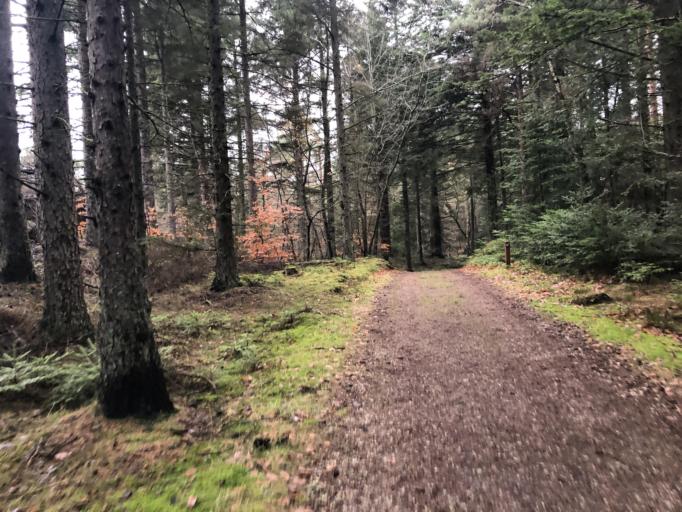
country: DK
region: Central Jutland
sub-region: Holstebro Kommune
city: Ulfborg
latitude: 56.2876
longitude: 8.1695
